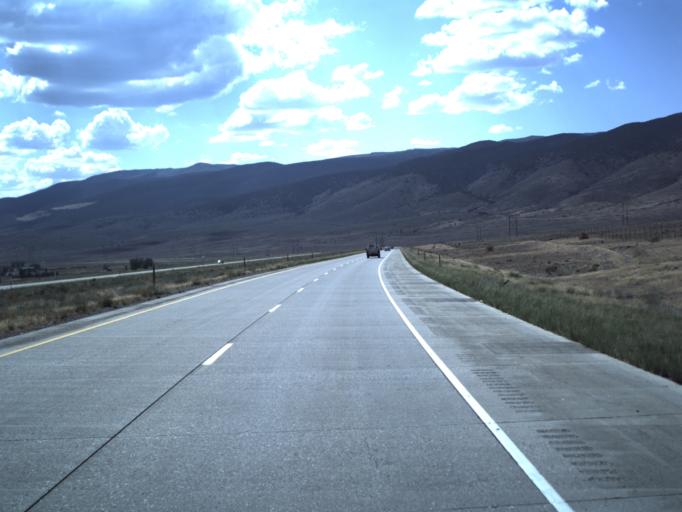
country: US
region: Utah
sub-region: Sevier County
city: Monroe
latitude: 38.6590
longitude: -112.1869
